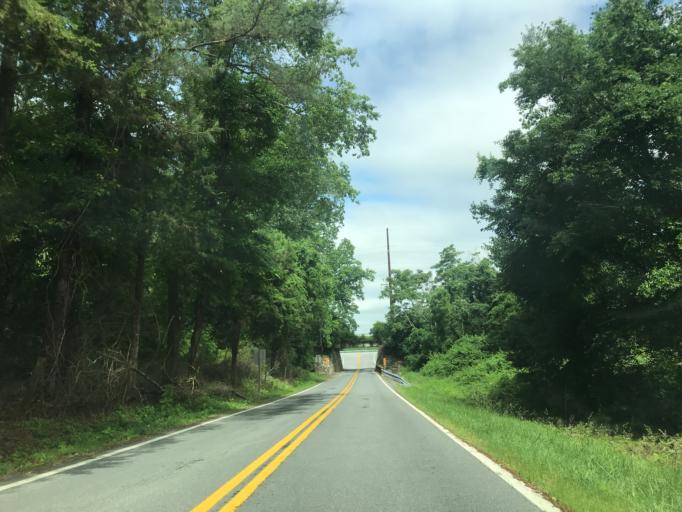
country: US
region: Maryland
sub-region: Caroline County
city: Ridgely
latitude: 38.8872
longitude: -75.9842
